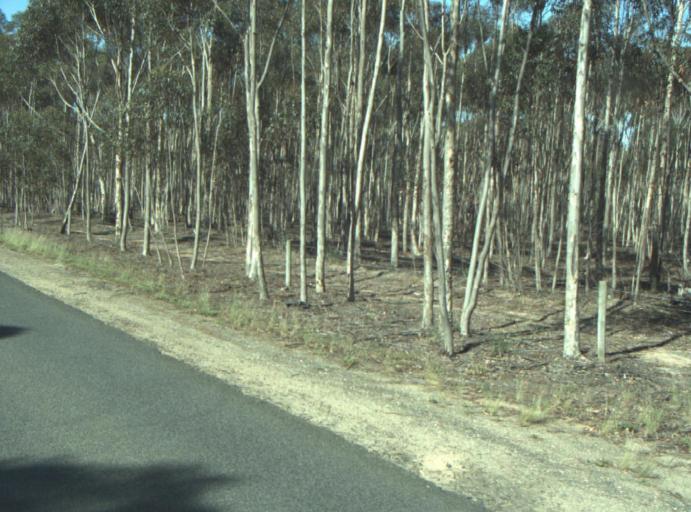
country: AU
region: Victoria
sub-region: Greater Geelong
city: Lara
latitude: -37.9447
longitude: 144.3919
